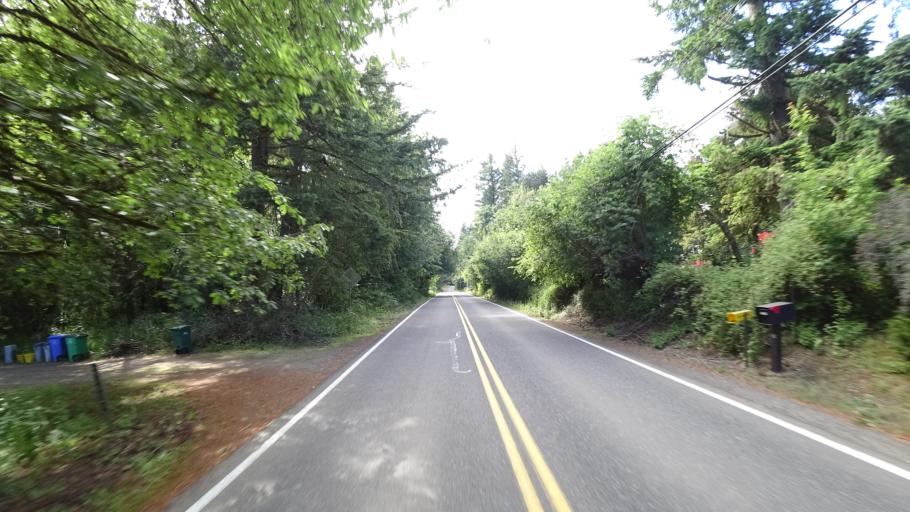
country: US
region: Oregon
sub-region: Washington County
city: Oak Hills
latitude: 45.5890
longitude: -122.8089
